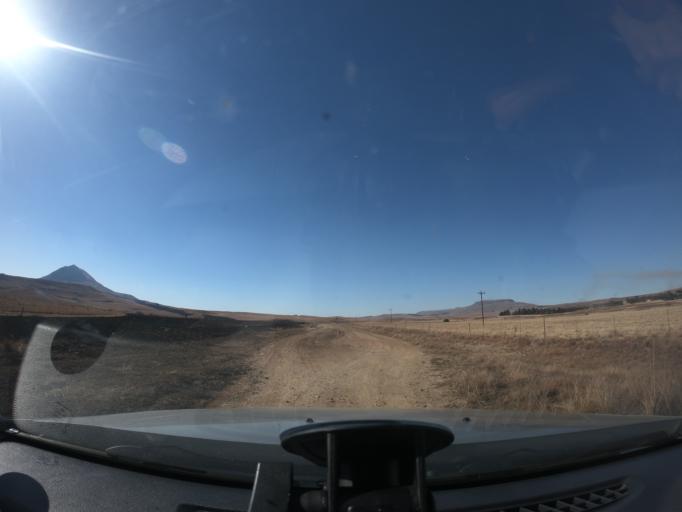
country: ZA
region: KwaZulu-Natal
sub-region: uMgungundlovu District Municipality
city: Impendle
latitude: -29.3886
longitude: 29.7336
